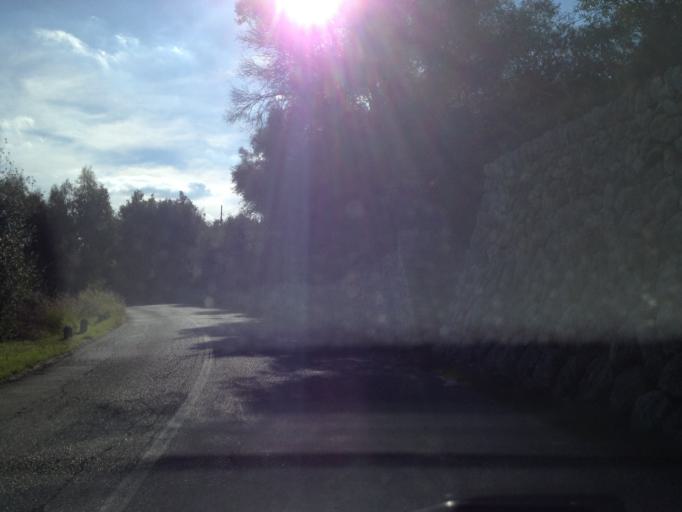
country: ES
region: Balearic Islands
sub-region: Illes Balears
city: Selva
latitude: 39.7479
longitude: 2.8995
